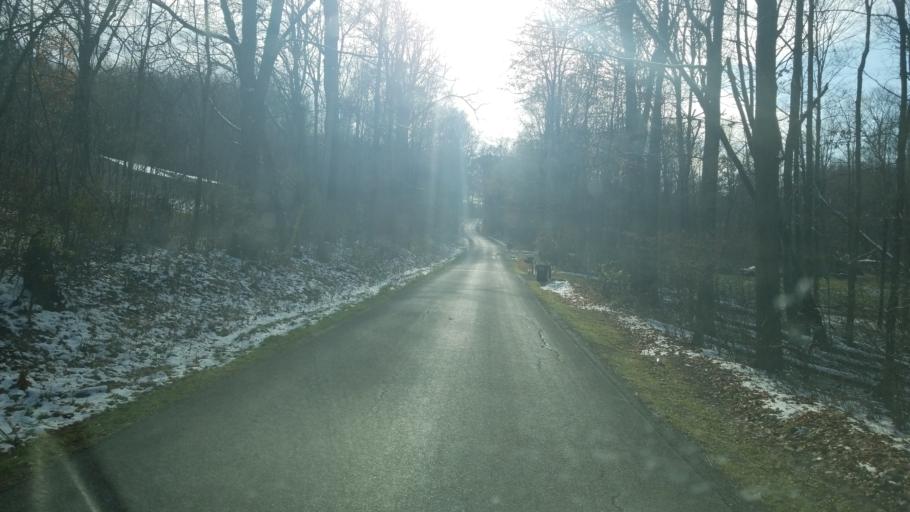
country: US
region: Ohio
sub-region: Licking County
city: Granville
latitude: 40.1492
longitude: -82.4851
